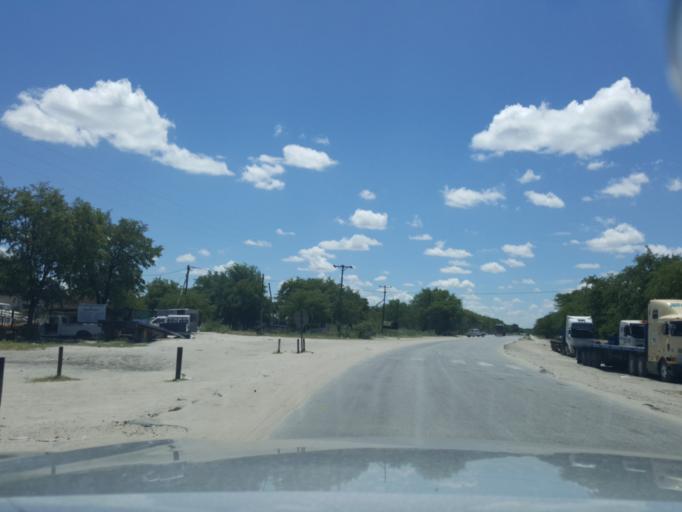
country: BW
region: Central
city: Nata
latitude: -20.2086
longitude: 26.1796
